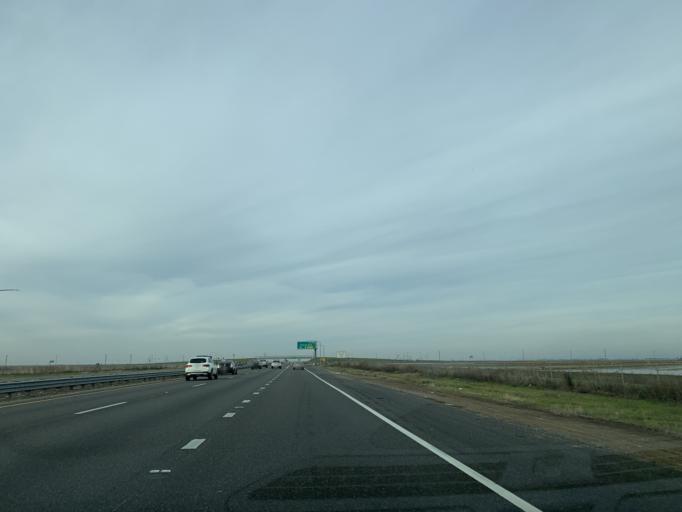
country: US
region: California
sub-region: Sacramento County
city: Elverta
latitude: 38.7068
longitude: -121.5402
